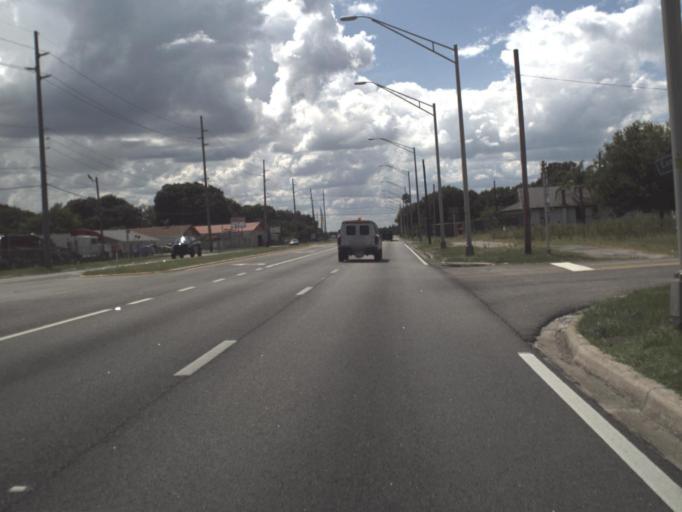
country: US
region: Florida
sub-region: Polk County
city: Lake Wales
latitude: 27.9037
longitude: -81.6243
